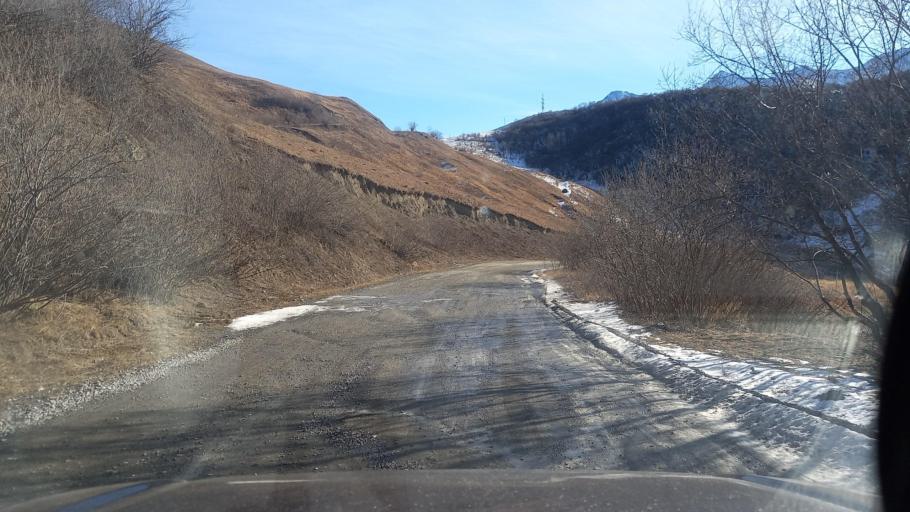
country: RU
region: North Ossetia
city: Verkhniy Fiagdon
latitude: 42.8366
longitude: 44.4717
